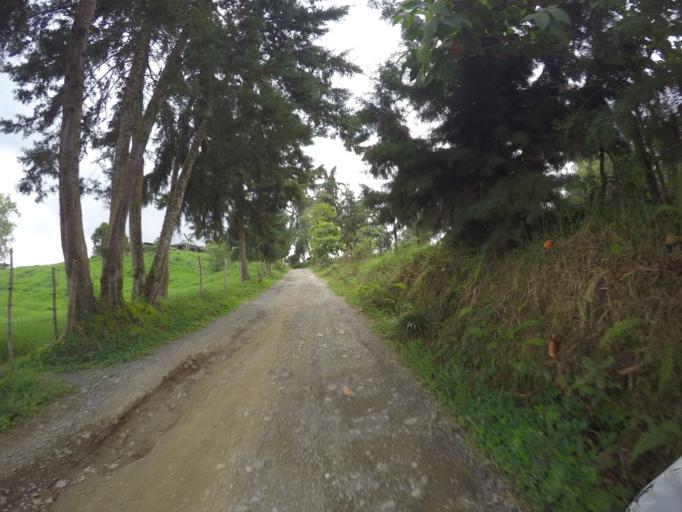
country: CO
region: Quindio
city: Filandia
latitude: 4.7122
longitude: -75.6424
